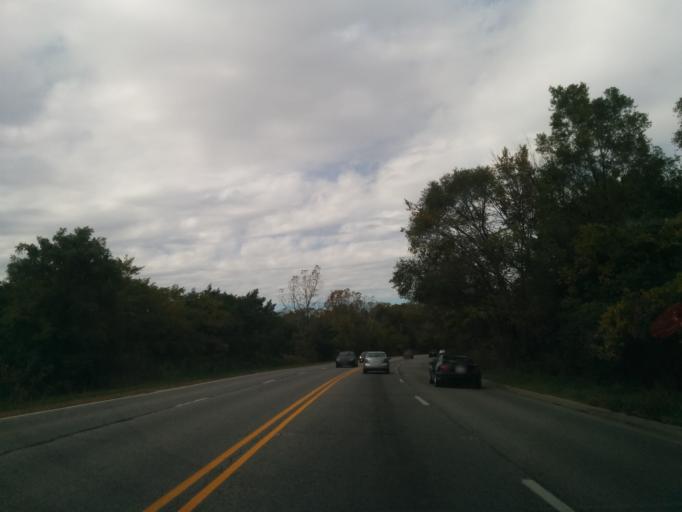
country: US
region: Illinois
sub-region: Cook County
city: River Grove
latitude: 41.9182
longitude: -87.8374
